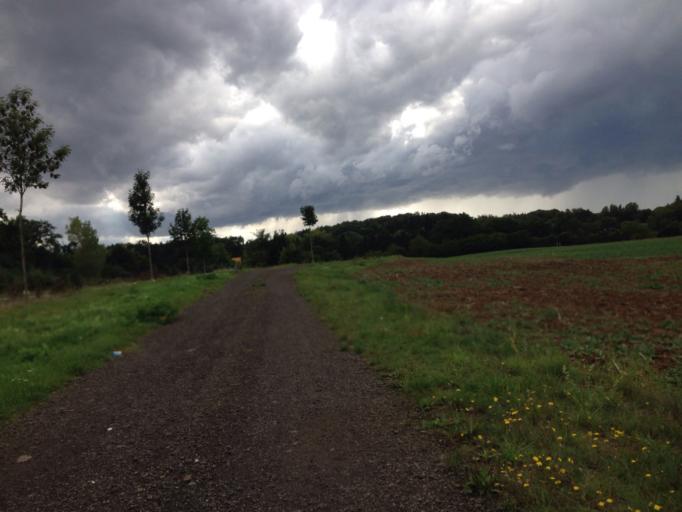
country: DE
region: Hesse
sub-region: Regierungsbezirk Giessen
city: Hungen
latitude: 50.4685
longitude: 8.9050
